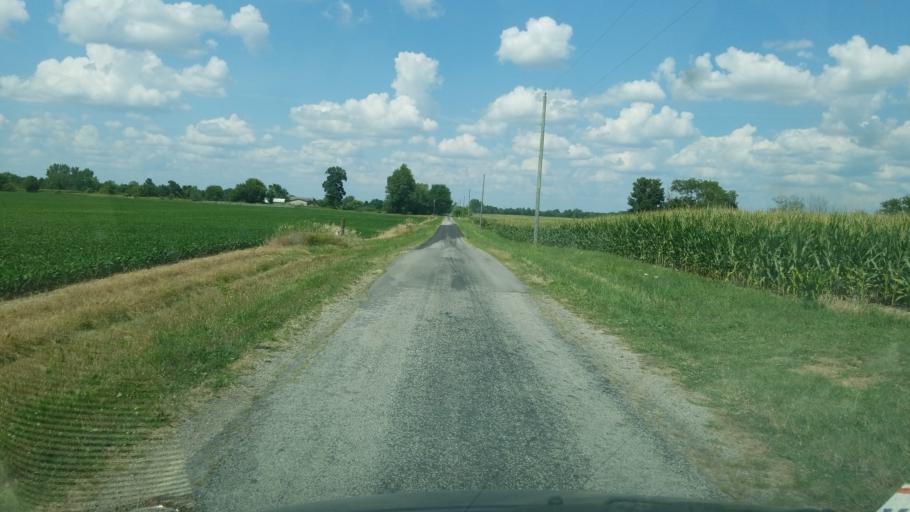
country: US
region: Ohio
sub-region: Union County
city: Richwood
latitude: 40.3949
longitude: -83.4737
